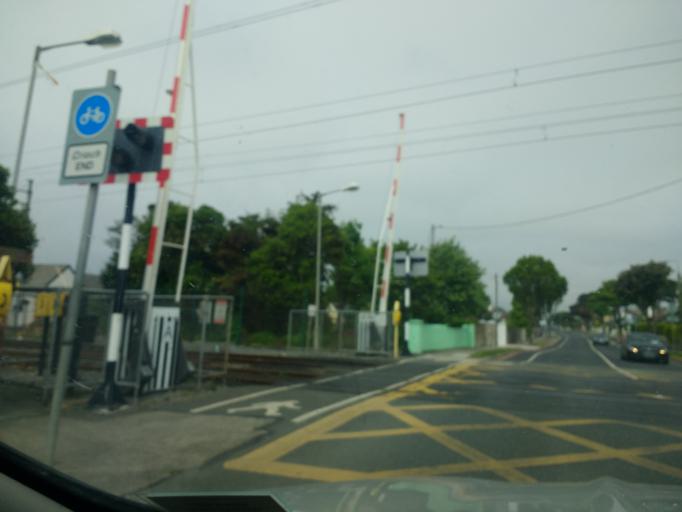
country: IE
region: Leinster
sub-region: Fingal County
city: Baldoyle
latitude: 53.3916
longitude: -6.1247
